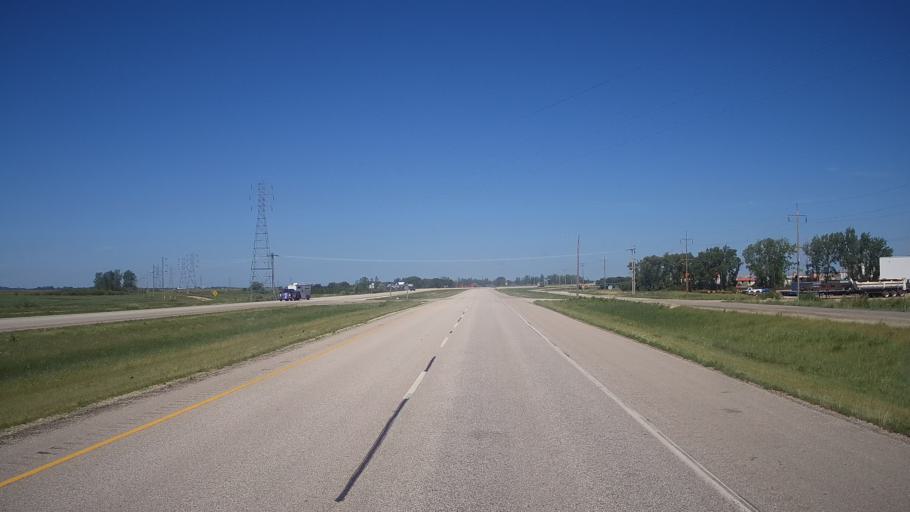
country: CA
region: Manitoba
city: Portage la Prairie
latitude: 49.9600
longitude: -98.3442
